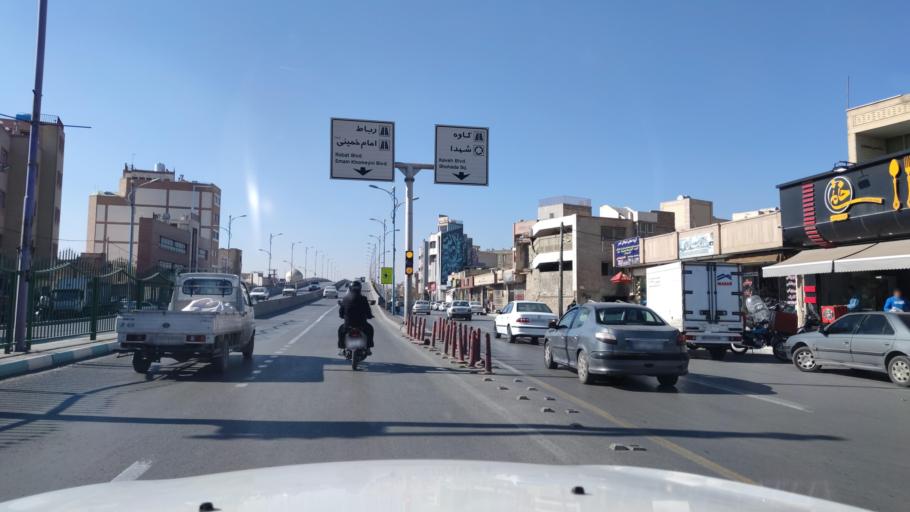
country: IR
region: Isfahan
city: Isfahan
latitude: 32.6790
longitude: 51.6755
